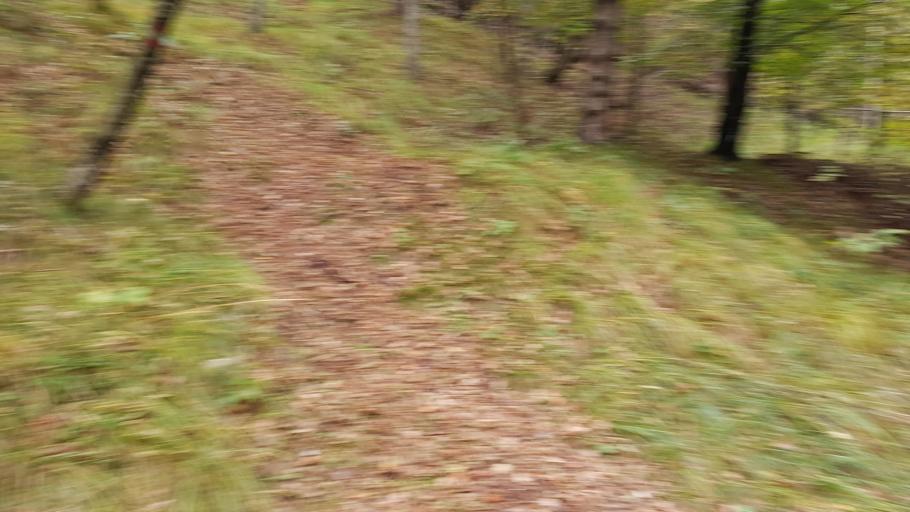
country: IT
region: Friuli Venezia Giulia
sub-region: Provincia di Udine
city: Chiusaforte
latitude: 46.4054
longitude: 13.3494
